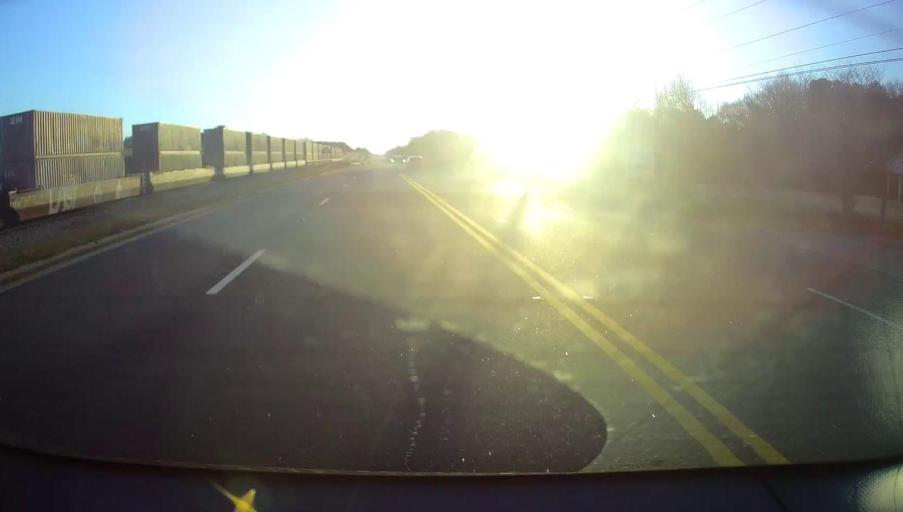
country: US
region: Georgia
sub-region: Fulton County
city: Fairburn
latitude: 33.5585
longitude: -84.5902
